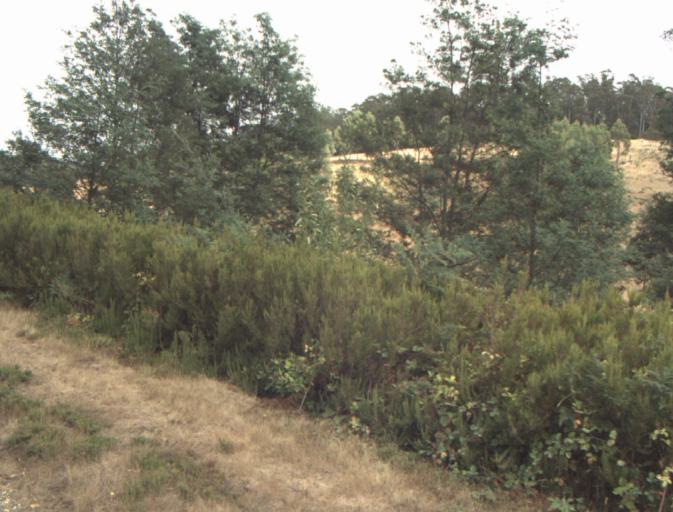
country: AU
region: Tasmania
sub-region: Dorset
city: Bridport
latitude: -41.1775
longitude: 147.2632
